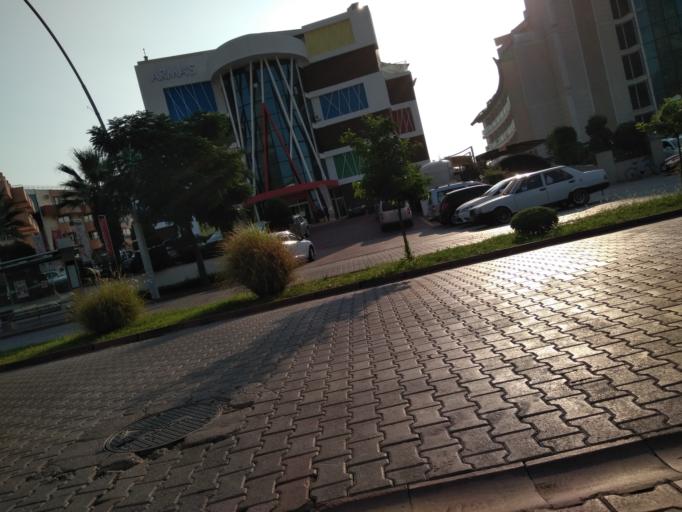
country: TR
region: Antalya
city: Kemer
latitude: 36.6149
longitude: 30.5559
